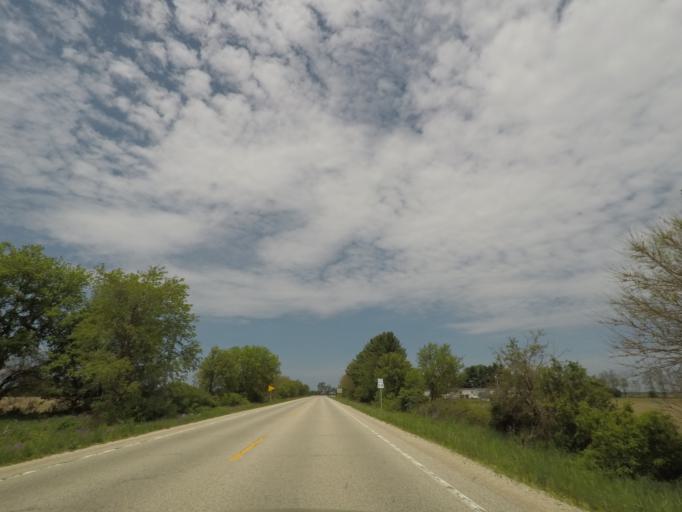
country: US
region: Wisconsin
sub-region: Rock County
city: Evansville
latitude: 42.7349
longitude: -89.2946
